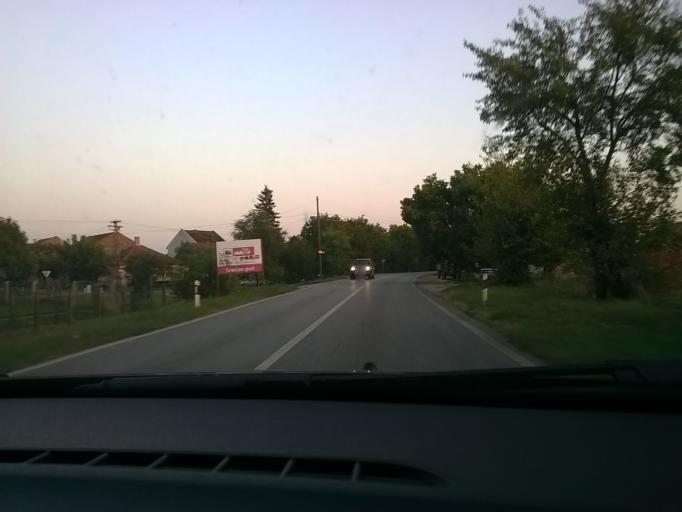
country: RS
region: Autonomna Pokrajina Vojvodina
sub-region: Juznobanatski Okrug
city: Vrsac
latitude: 45.1063
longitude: 21.2979
